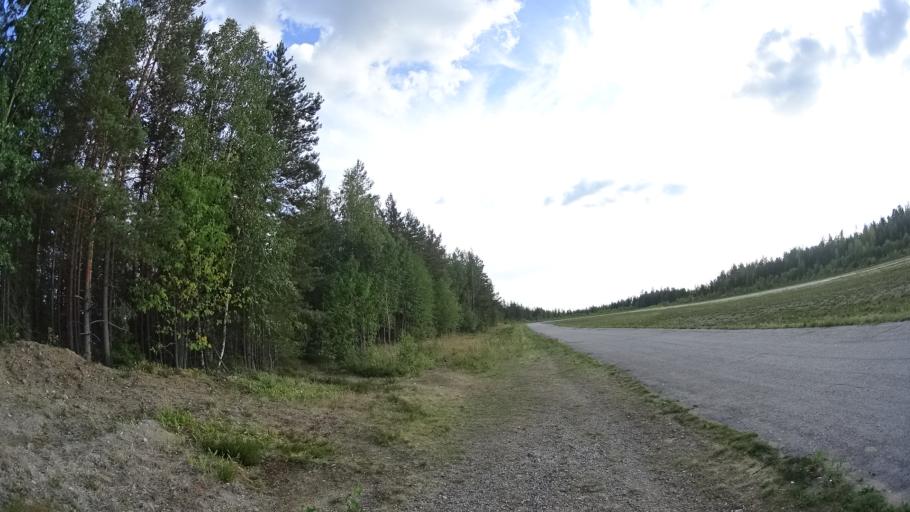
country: FI
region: Uusimaa
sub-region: Helsinki
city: Vihti
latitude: 60.3283
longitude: 24.2867
